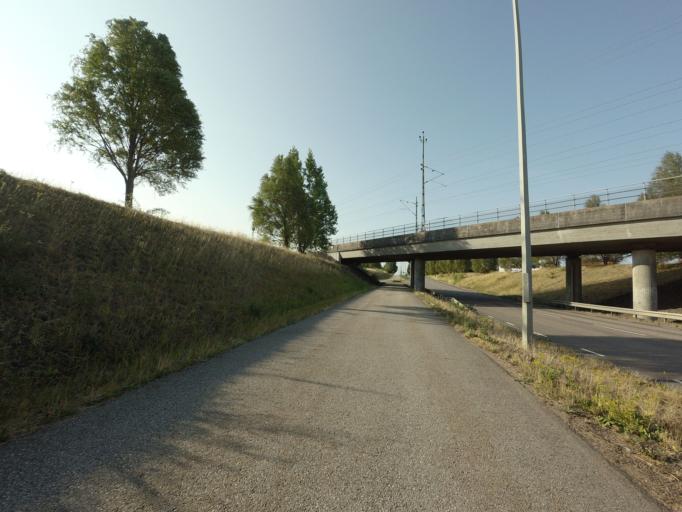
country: SE
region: Skane
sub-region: Landskrona
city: Landskrona
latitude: 55.8693
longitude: 12.8694
